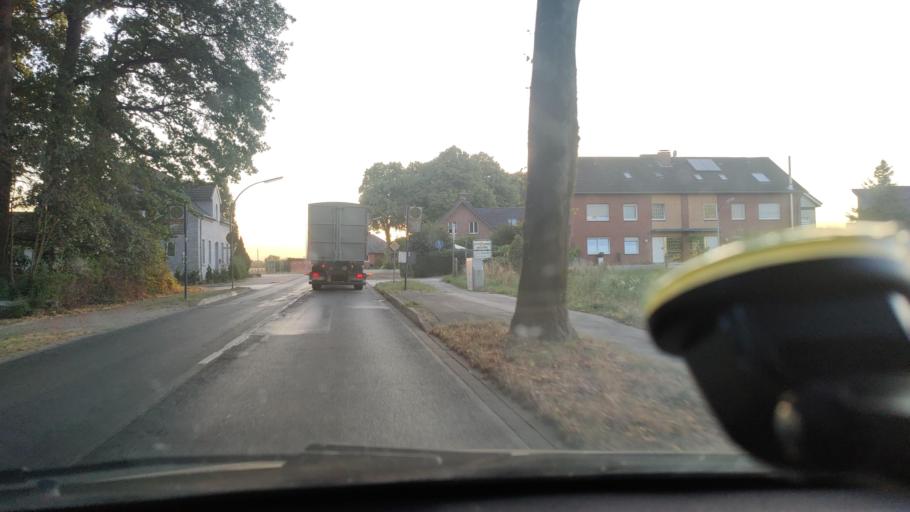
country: DE
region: North Rhine-Westphalia
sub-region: Regierungsbezirk Munster
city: Raesfeld
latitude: 51.7518
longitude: 6.9261
